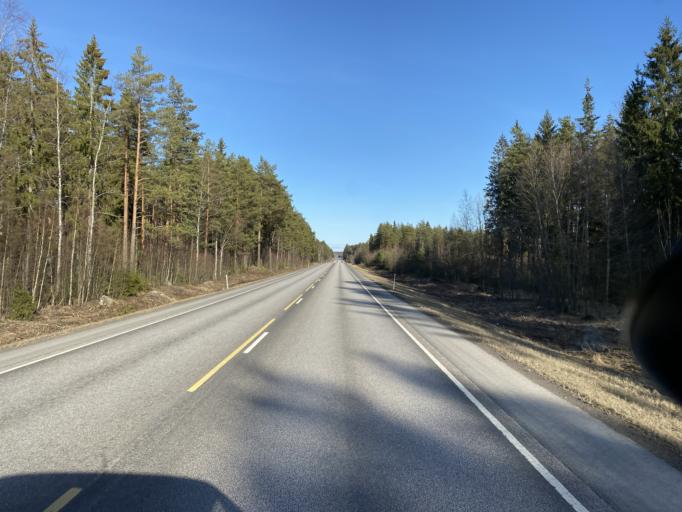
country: FI
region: Satakunta
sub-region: Rauma
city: Eura
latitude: 61.1313
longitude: 22.0919
